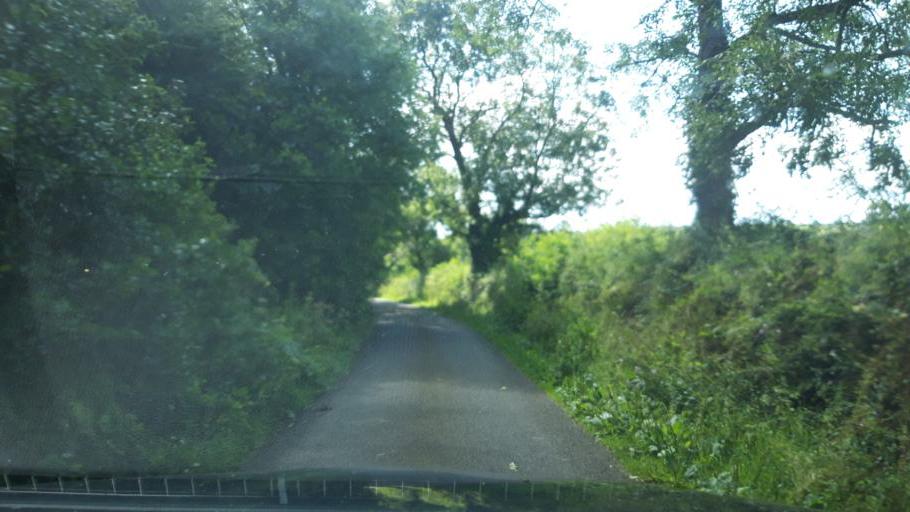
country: IE
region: Leinster
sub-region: Kilkenny
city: Graiguenamanagh
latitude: 52.5807
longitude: -6.9897
